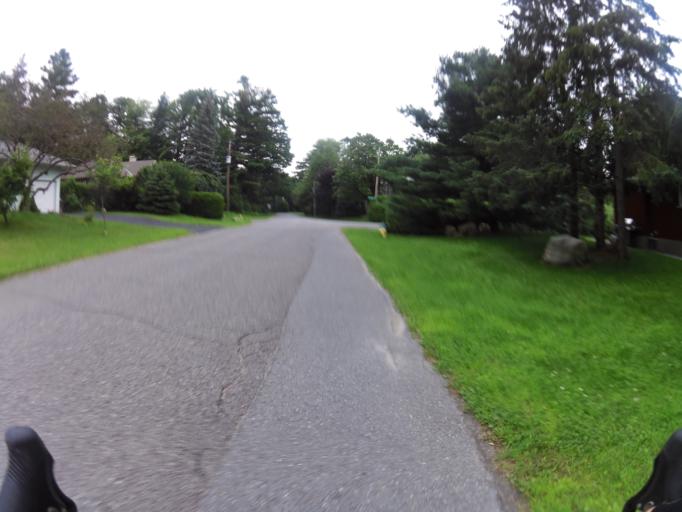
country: CA
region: Ontario
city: Ottawa
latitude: 45.3254
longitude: -75.7119
